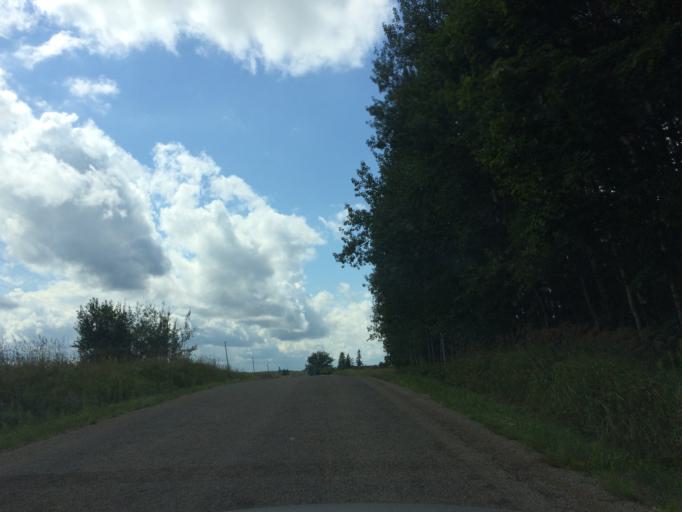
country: LV
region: Rezekne
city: Rezekne
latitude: 56.5613
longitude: 27.4417
